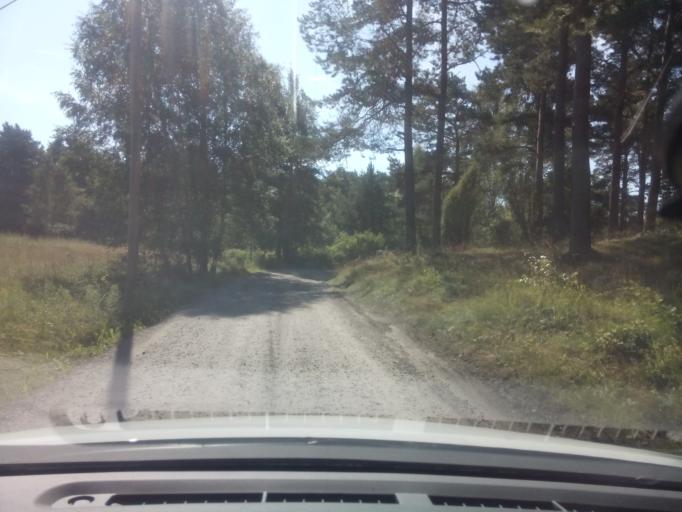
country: SE
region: Soedermanland
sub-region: Oxelosunds Kommun
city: Oxelosund
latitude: 58.7291
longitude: 17.2490
